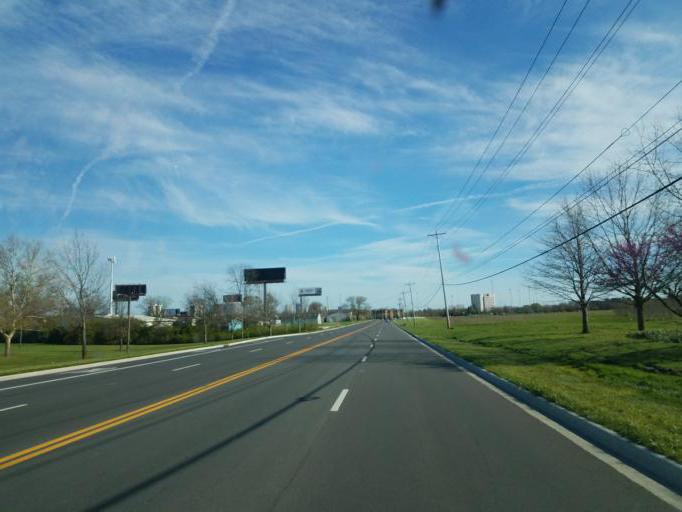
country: US
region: Ohio
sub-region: Franklin County
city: Upper Arlington
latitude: 40.0115
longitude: -83.0365
